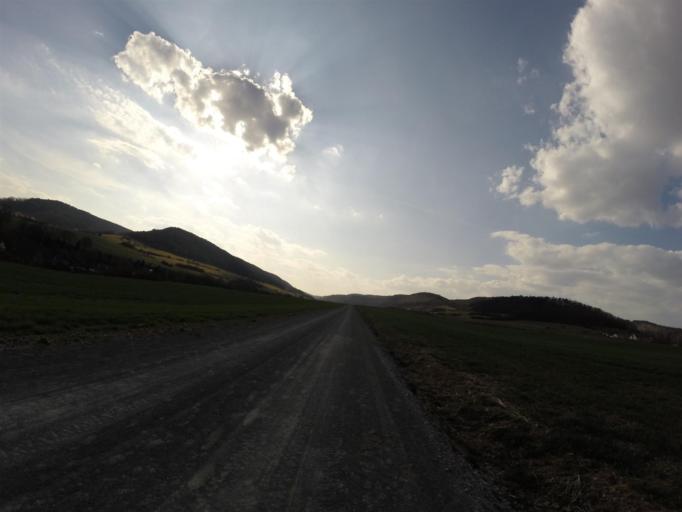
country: DE
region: Thuringia
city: Rothenstein
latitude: 50.8695
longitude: 11.5946
